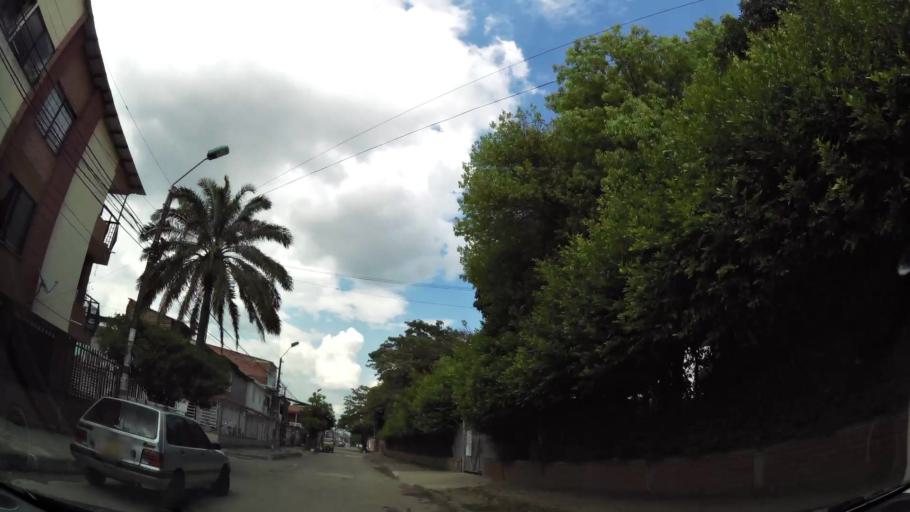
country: CO
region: Valle del Cauca
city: Cali
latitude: 3.4067
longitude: -76.5189
